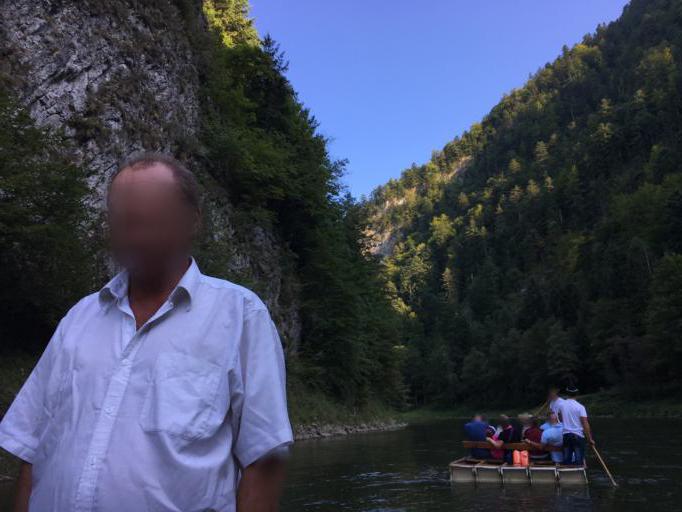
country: PL
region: Lesser Poland Voivodeship
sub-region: Powiat nowotarski
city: Kroscienko nad Dunajcem
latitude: 49.4130
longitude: 20.4442
